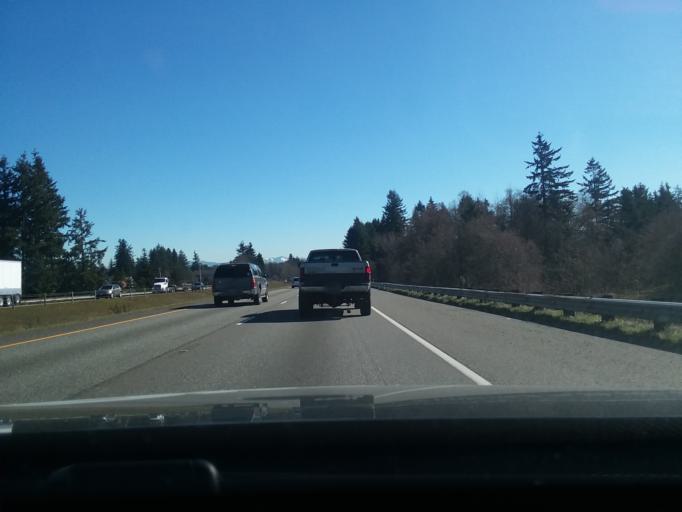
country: US
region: Washington
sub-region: Pierce County
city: Summit
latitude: 47.1582
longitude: -122.3274
